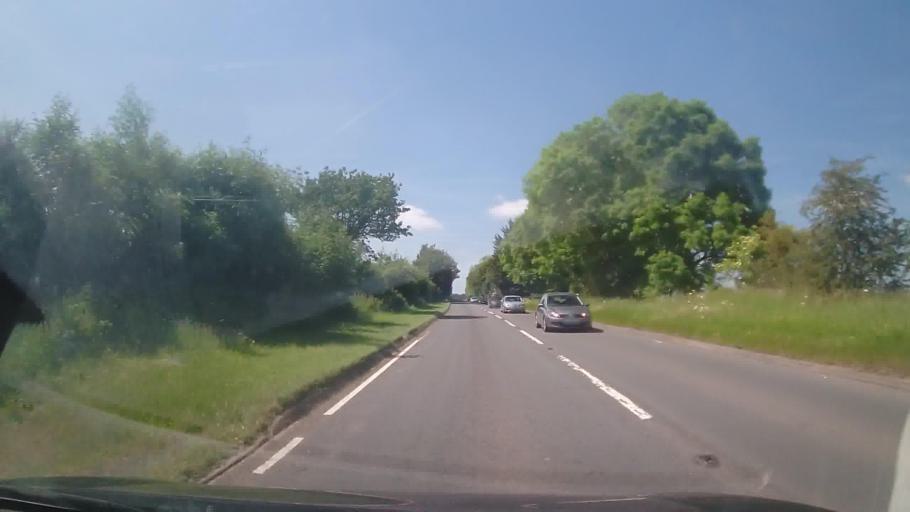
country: GB
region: England
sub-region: Herefordshire
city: Kimbolton
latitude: 52.2918
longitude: -2.7010
